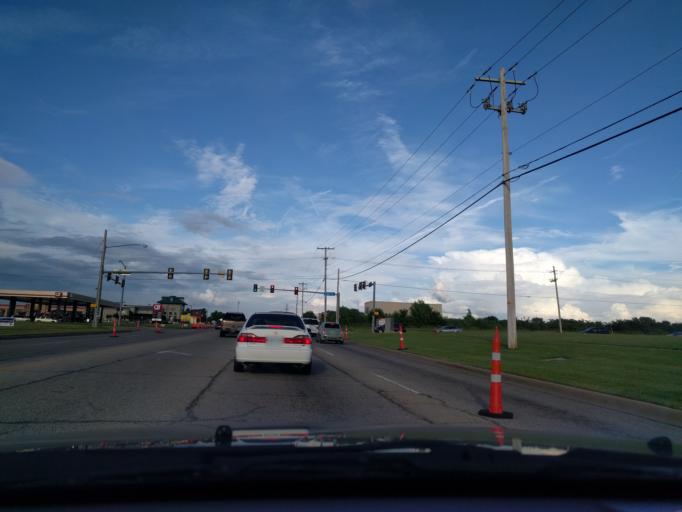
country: US
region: Oklahoma
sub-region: Tulsa County
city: Broken Arrow
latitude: 36.0609
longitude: -95.8339
